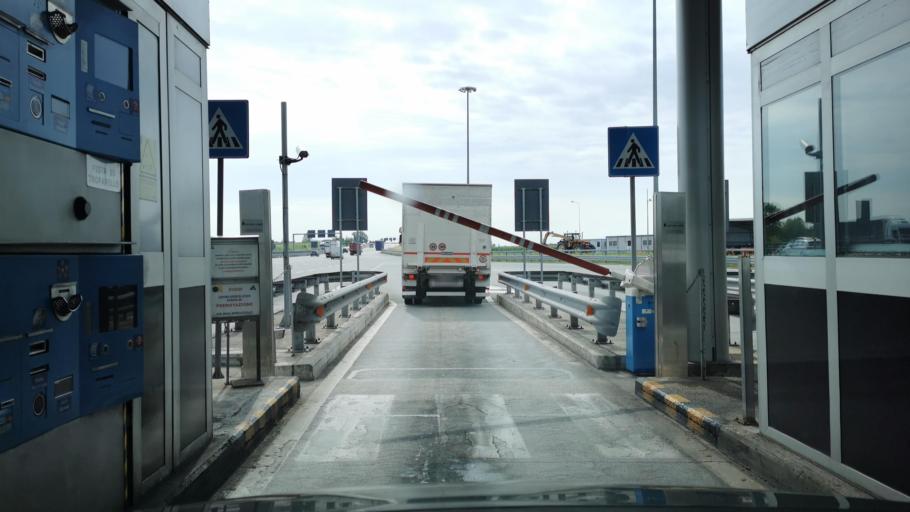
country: IT
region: Piedmont
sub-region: Provincia di Torino
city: Trofarello
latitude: 44.9658
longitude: 7.7368
